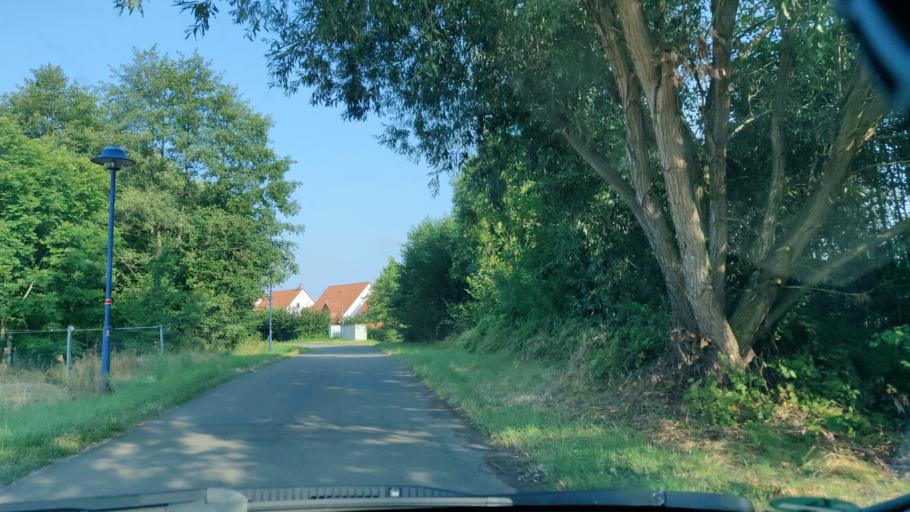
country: DE
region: Saxony
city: Bad Lausick
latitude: 51.1383
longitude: 12.6471
